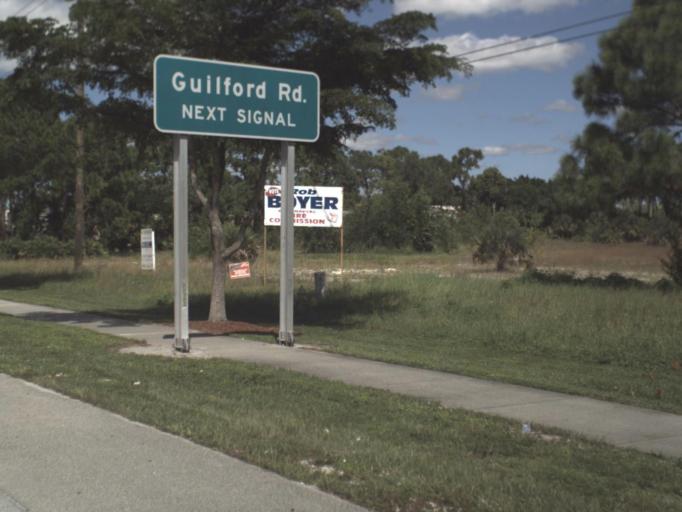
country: US
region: Florida
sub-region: Collier County
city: Lely
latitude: 26.1168
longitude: -81.7565
